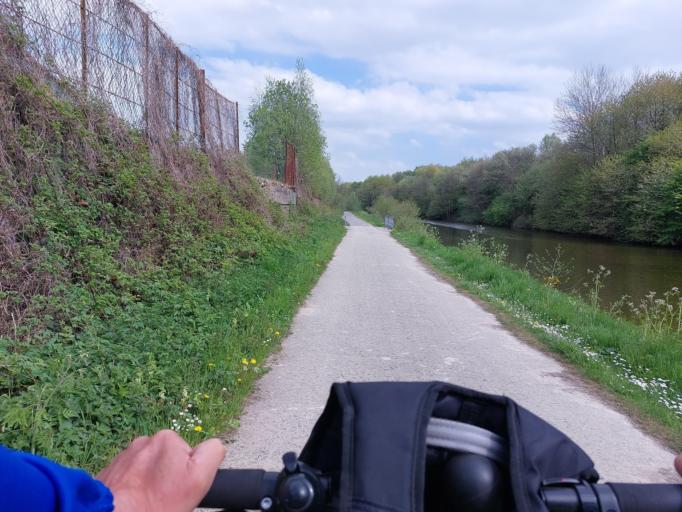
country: FR
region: Nord-Pas-de-Calais
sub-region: Departement du Nord
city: Hautmont
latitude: 50.2629
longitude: 3.9332
